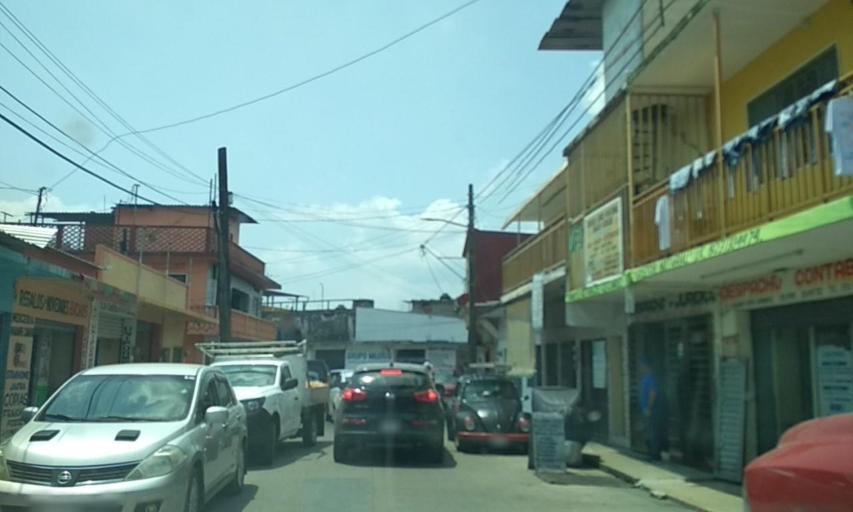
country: MX
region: Veracruz
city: Las Choapas
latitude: 17.9105
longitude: -94.0895
